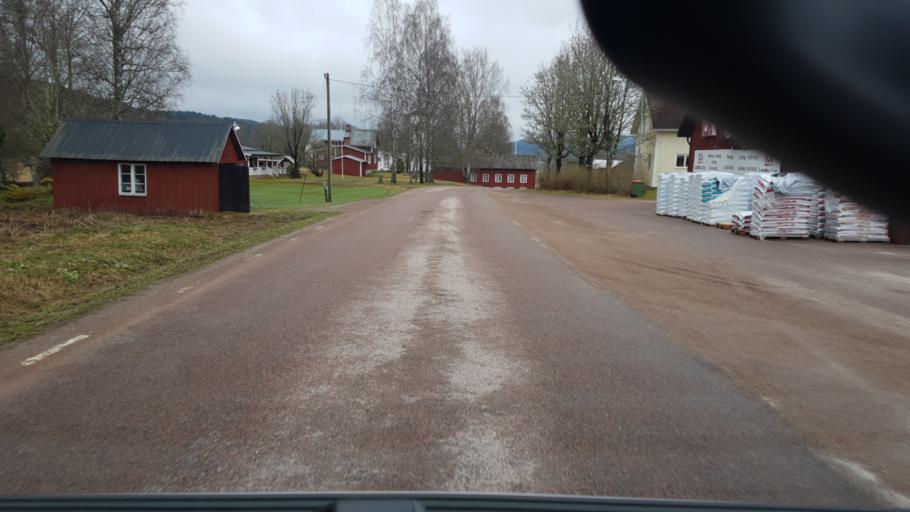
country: SE
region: Vaermland
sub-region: Arvika Kommun
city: Arvika
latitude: 59.7535
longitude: 12.8236
